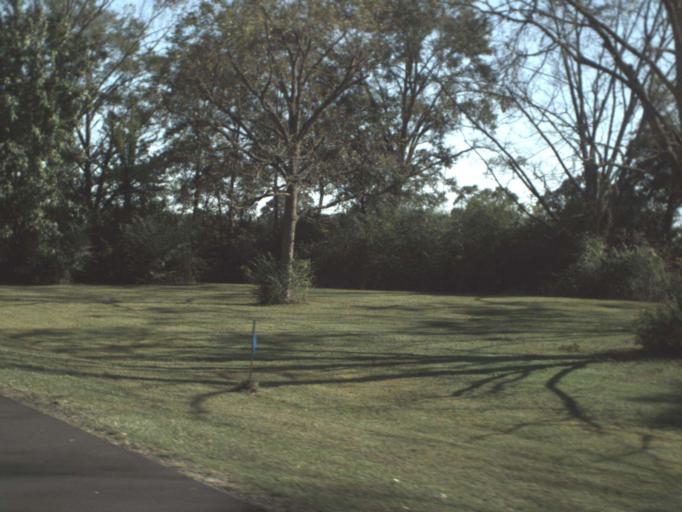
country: US
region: Florida
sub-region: Walton County
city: DeFuniak Springs
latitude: 30.8245
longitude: -86.2261
